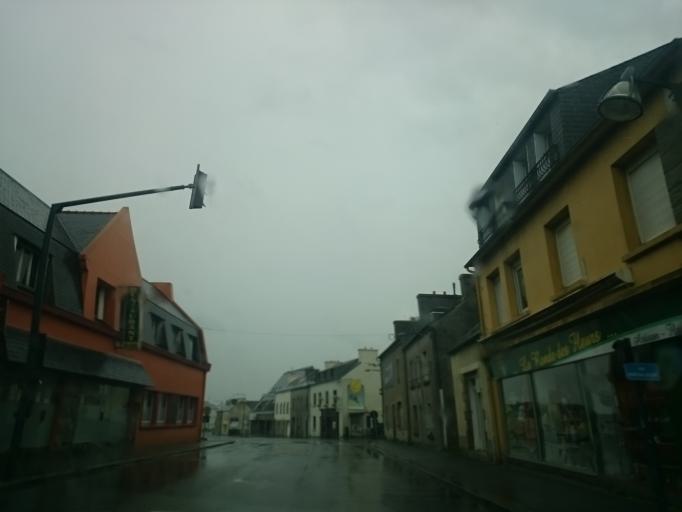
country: FR
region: Brittany
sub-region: Departement du Finistere
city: Plabennec
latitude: 48.5023
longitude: -4.4261
